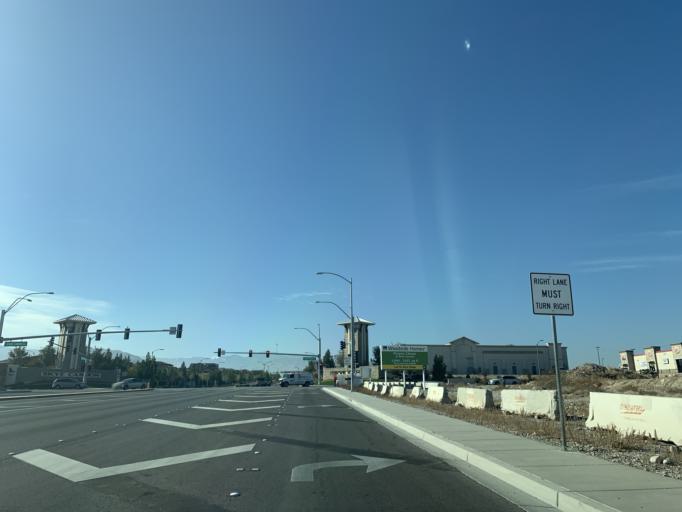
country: US
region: Nevada
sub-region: Clark County
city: Summerlin South
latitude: 36.3142
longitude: -115.3050
